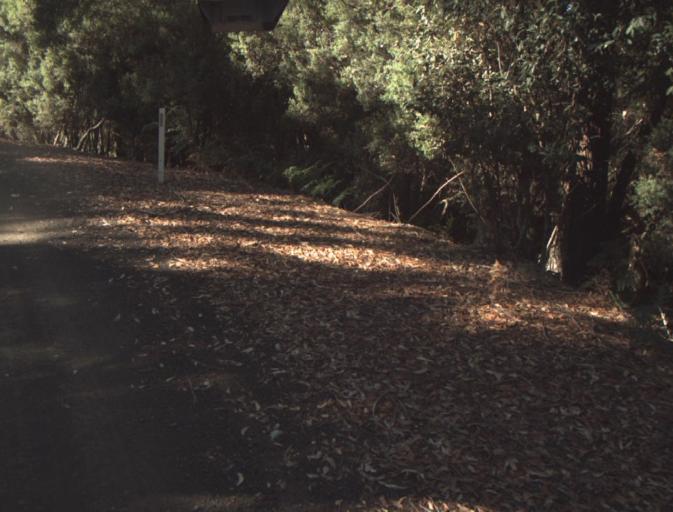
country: AU
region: Tasmania
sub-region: Dorset
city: Scottsdale
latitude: -41.2935
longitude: 147.3540
